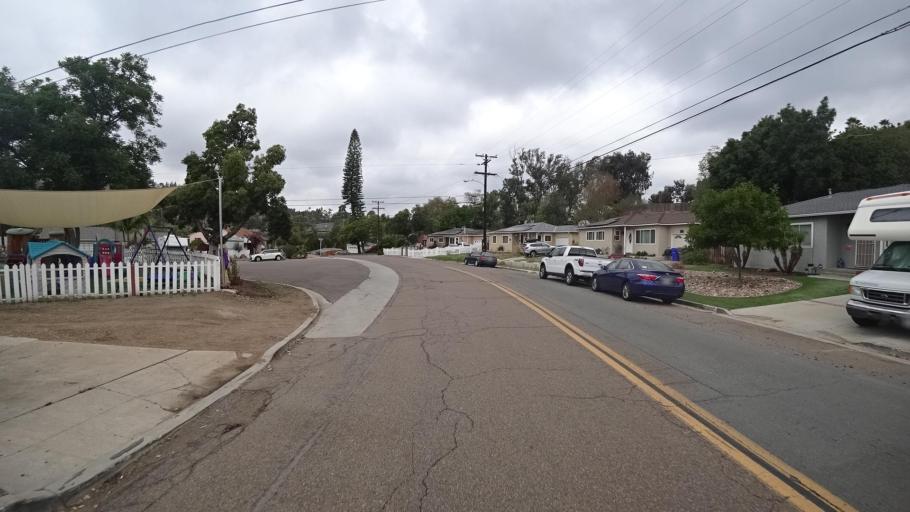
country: US
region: California
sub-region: San Diego County
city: Spring Valley
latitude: 32.7490
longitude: -117.0124
